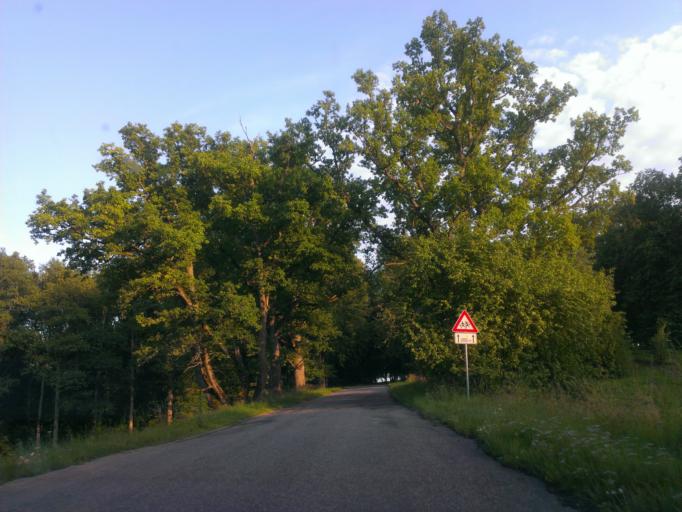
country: LV
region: Amatas Novads
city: Drabesi
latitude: 57.2452
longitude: 25.2811
